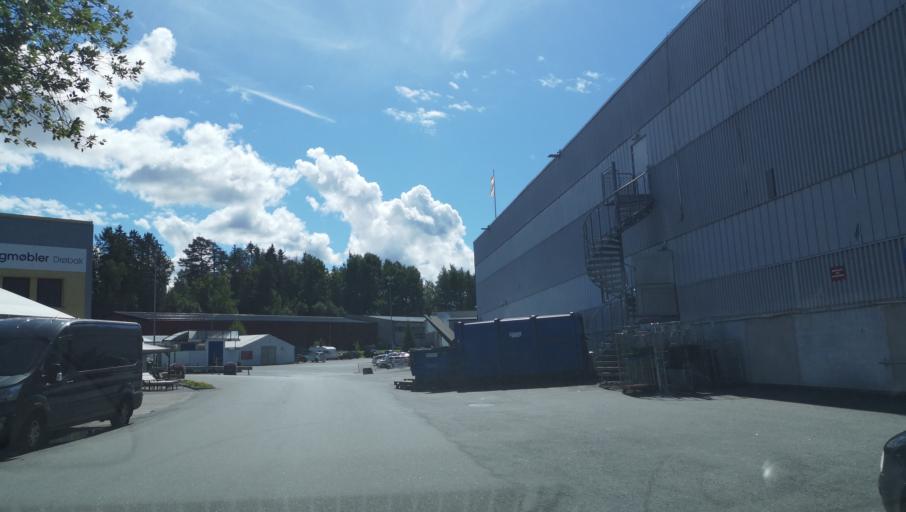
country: NO
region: Akershus
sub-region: Frogn
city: Drobak
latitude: 59.6727
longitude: 10.6590
